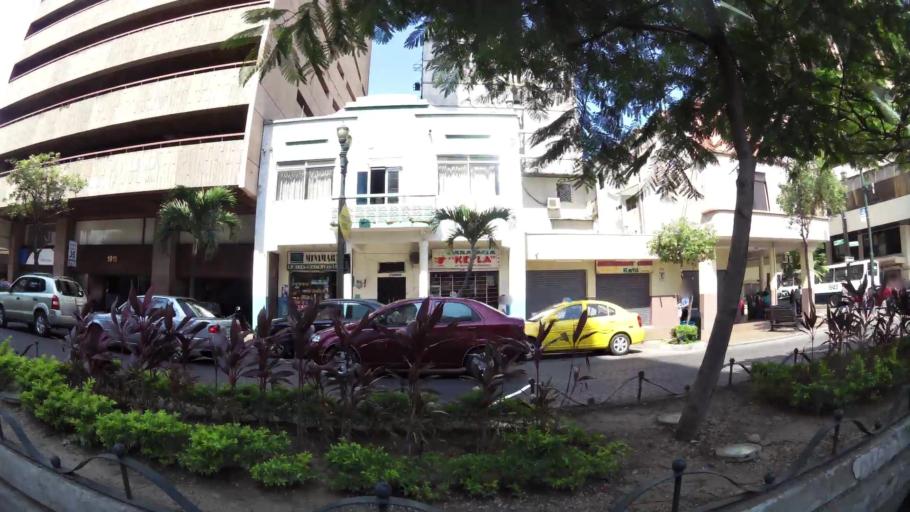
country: EC
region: Guayas
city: Guayaquil
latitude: -2.1878
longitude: -79.8937
